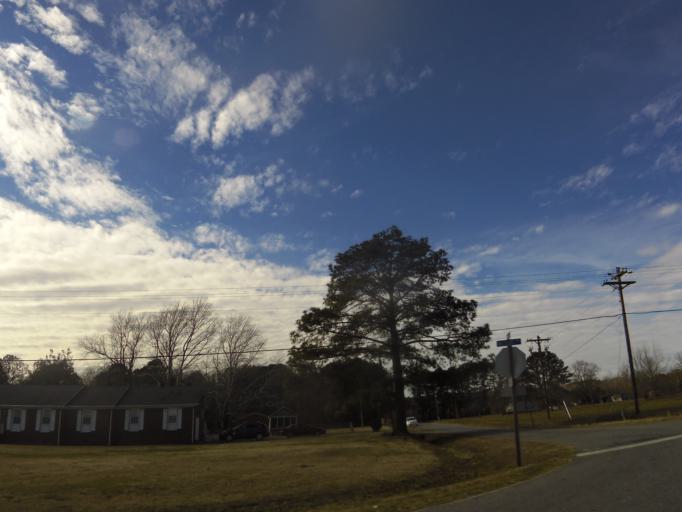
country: US
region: Virginia
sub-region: City of Franklin
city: Franklin
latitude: 36.7204
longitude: -76.8829
